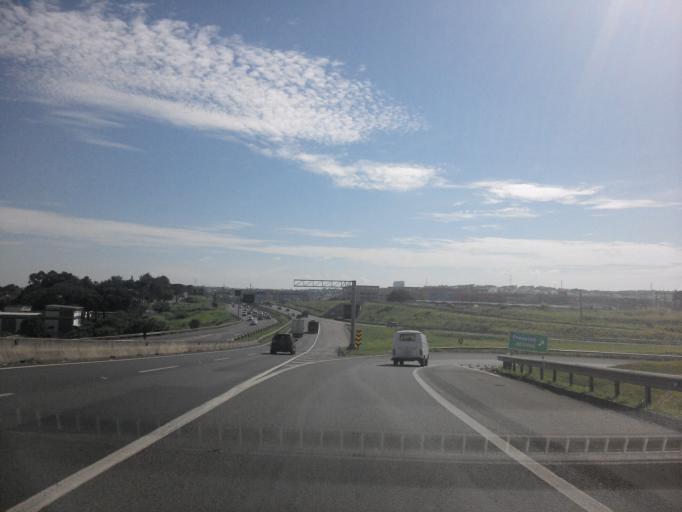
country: BR
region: Sao Paulo
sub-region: Campinas
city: Campinas
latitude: -22.8436
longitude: -47.0380
